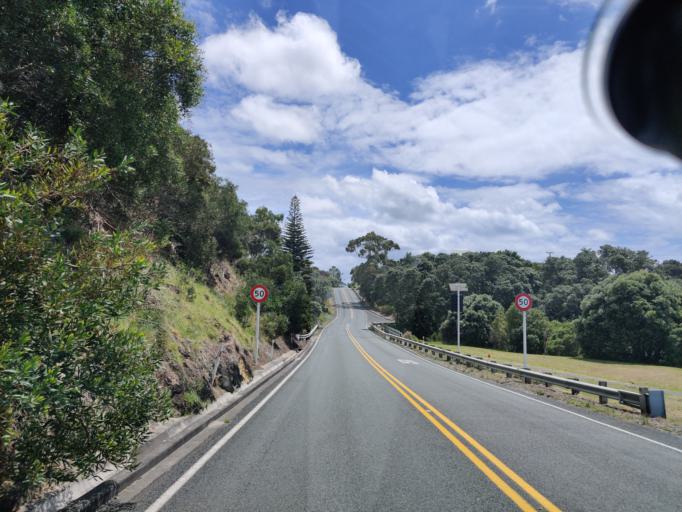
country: NZ
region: Northland
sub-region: Far North District
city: Kaitaia
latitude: -34.8118
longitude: 173.1165
